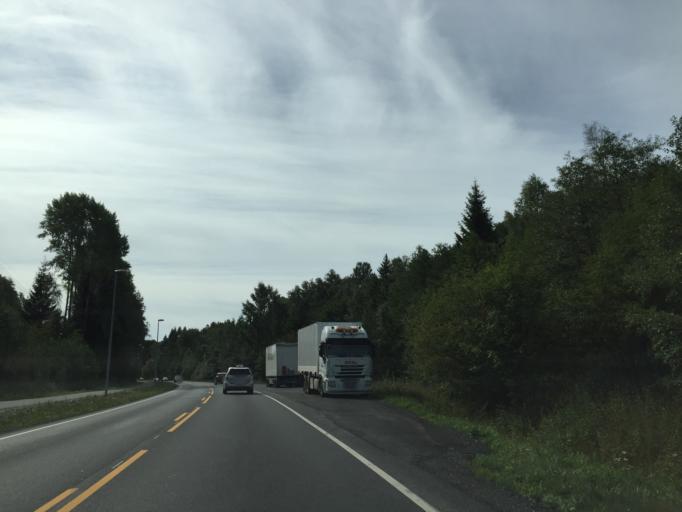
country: NO
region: Ostfold
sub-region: Moss
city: Moss
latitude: 59.4590
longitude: 10.6871
